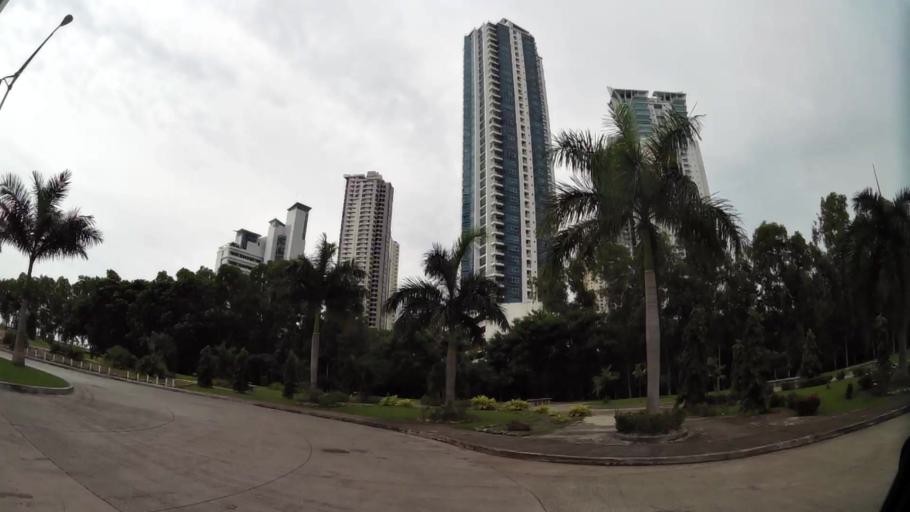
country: PA
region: Panama
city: San Miguelito
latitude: 9.0113
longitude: -79.4685
